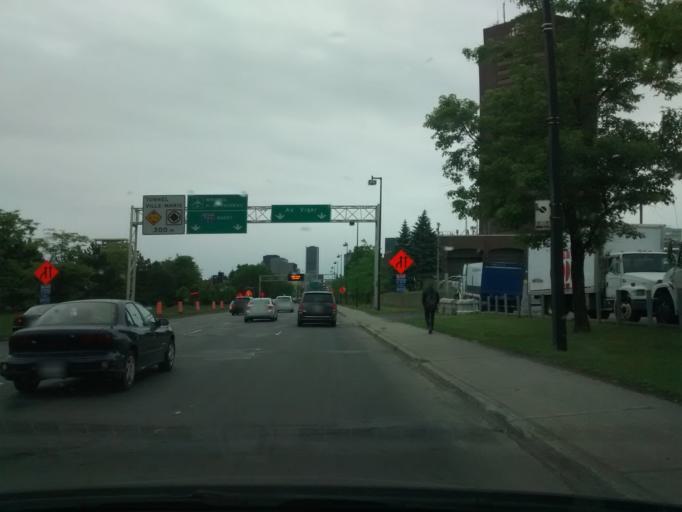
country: CA
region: Quebec
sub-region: Monteregie
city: Longueuil
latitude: 45.5198
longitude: -73.5486
